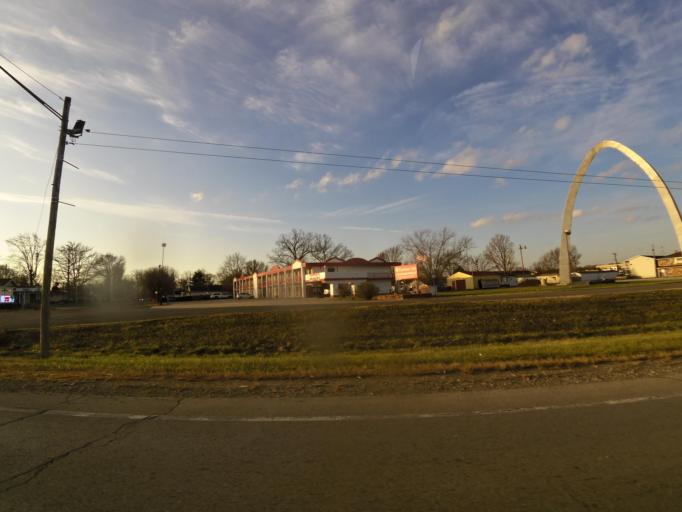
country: US
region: Illinois
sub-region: Fayette County
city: Vandalia
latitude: 38.9769
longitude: -89.0974
